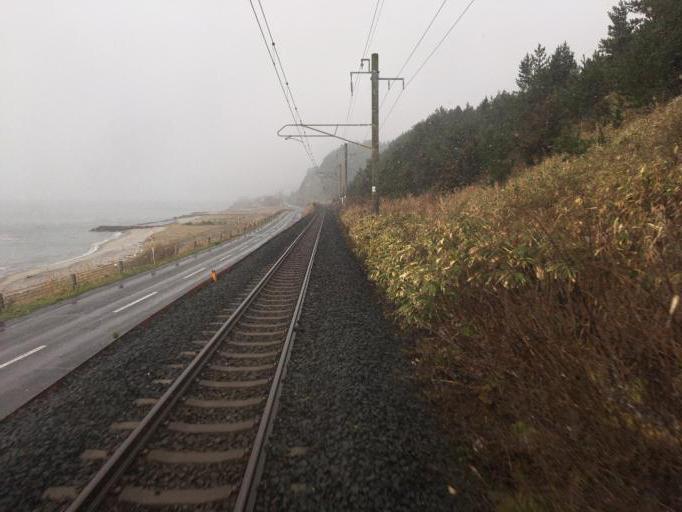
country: JP
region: Aomori
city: Aomori Shi
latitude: 41.0270
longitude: 140.6467
